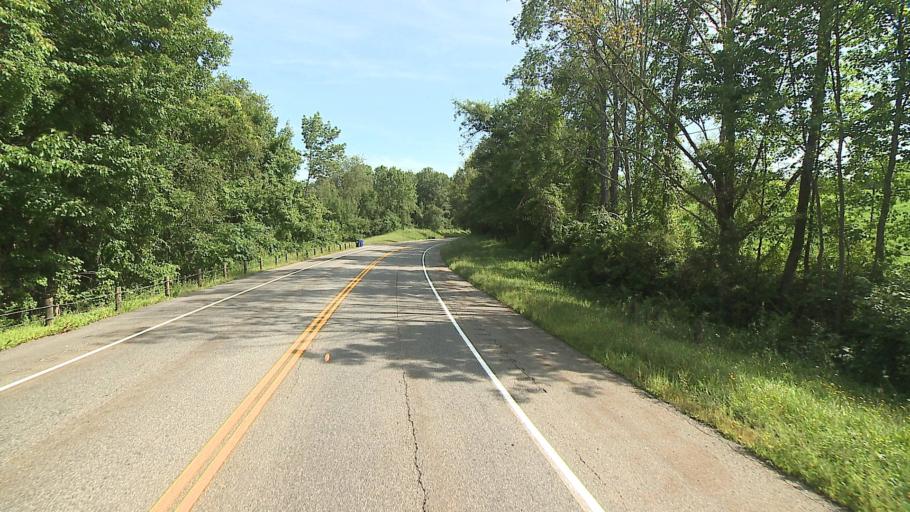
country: US
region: Connecticut
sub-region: Litchfield County
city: Litchfield
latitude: 41.7593
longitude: -73.1578
